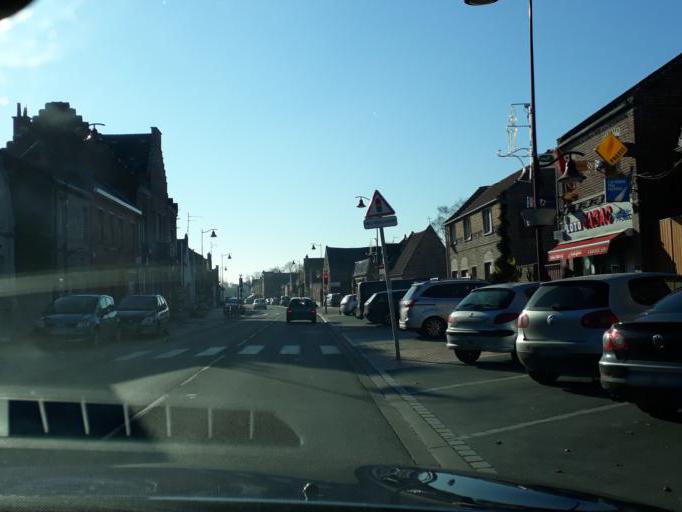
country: FR
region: Nord-Pas-de-Calais
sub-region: Departement du Nord
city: Masny
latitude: 50.3485
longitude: 3.2012
